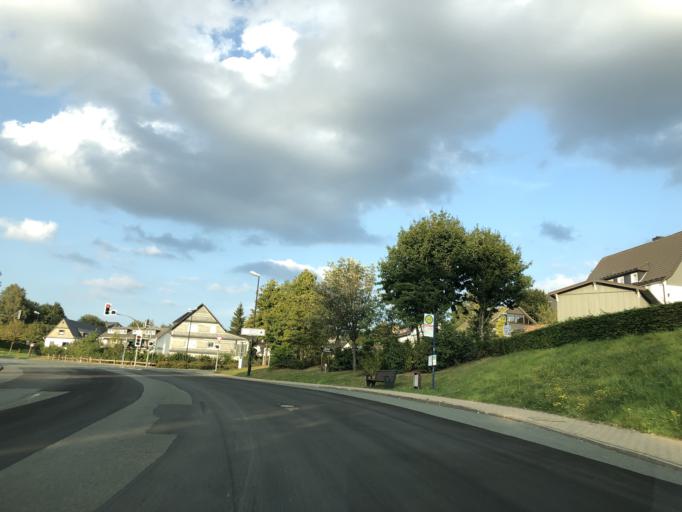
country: DE
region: North Rhine-Westphalia
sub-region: Regierungsbezirk Arnsberg
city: Winterberg
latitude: 51.1910
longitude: 8.5299
